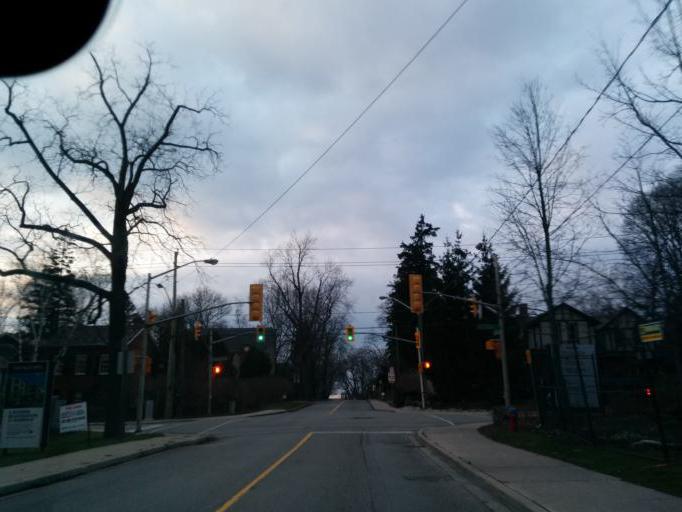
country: CA
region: Ontario
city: Oakville
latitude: 43.4536
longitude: -79.6752
